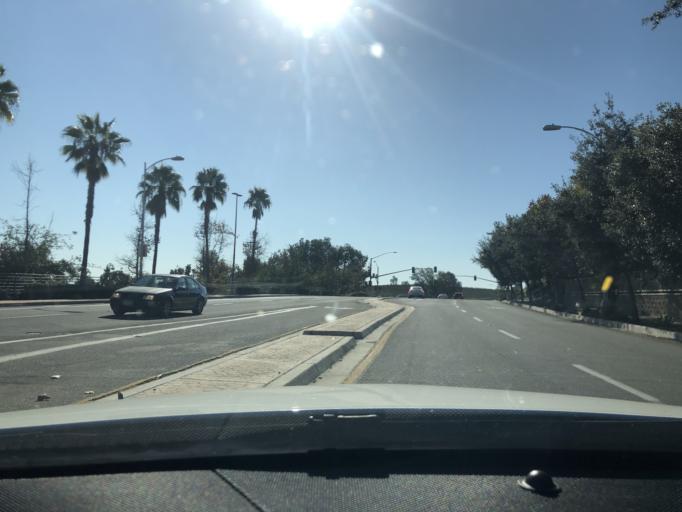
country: US
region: California
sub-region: San Diego County
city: Lemon Grove
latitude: 32.7393
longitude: -117.0575
